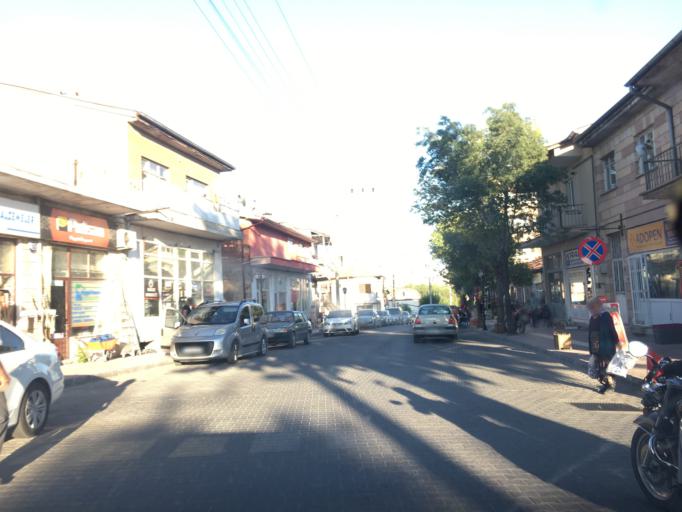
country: TR
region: Nevsehir
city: Avanos
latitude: 38.7177
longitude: 34.8424
